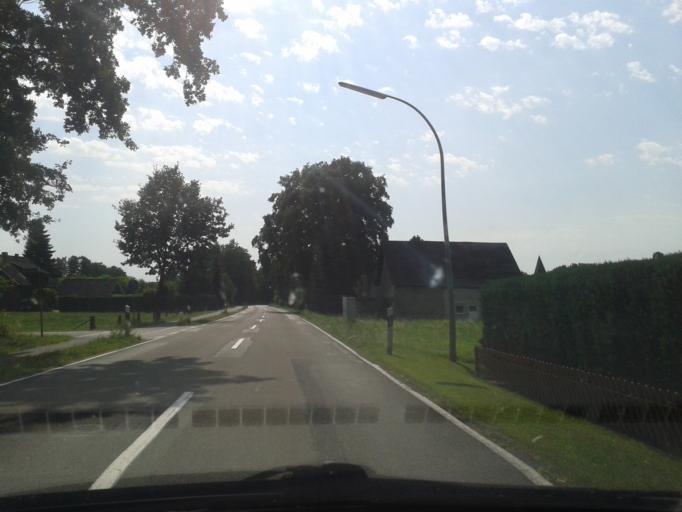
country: DE
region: North Rhine-Westphalia
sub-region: Regierungsbezirk Detmold
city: Hovelhof
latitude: 51.8753
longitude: 8.6190
